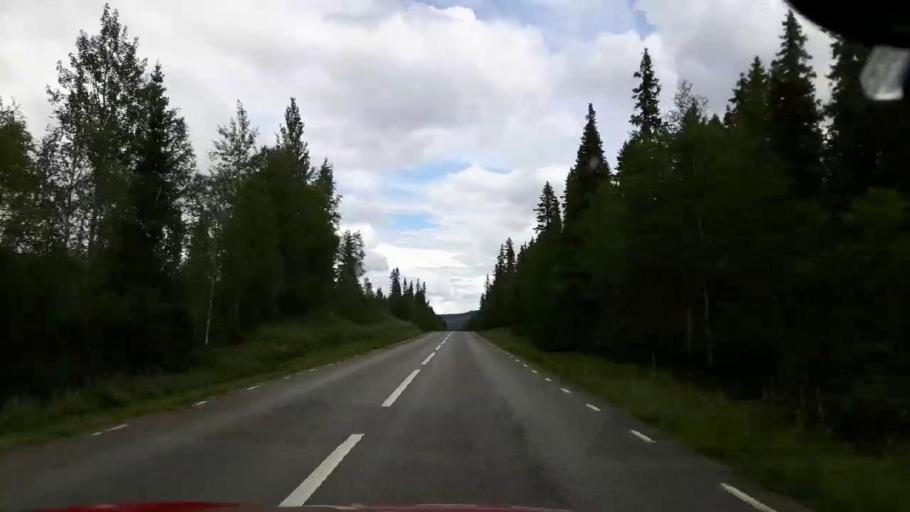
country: NO
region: Nord-Trondelag
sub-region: Lierne
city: Sandvika
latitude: 64.3901
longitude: 14.4501
